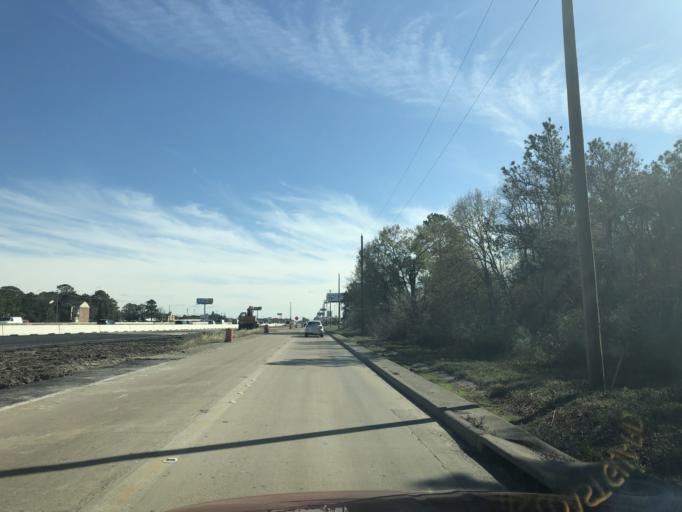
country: US
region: Texas
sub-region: Galveston County
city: Dickinson
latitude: 29.4604
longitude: -95.0867
